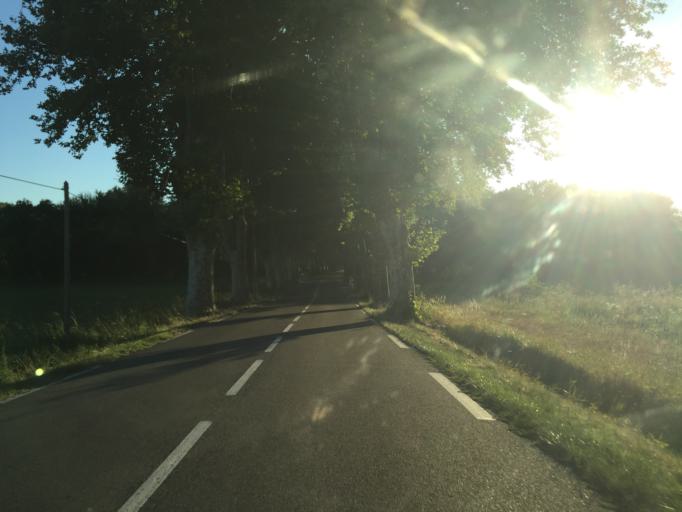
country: FR
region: Provence-Alpes-Cote d'Azur
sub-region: Departement des Alpes-de-Haute-Provence
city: Cereste
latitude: 43.8583
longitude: 5.6148
